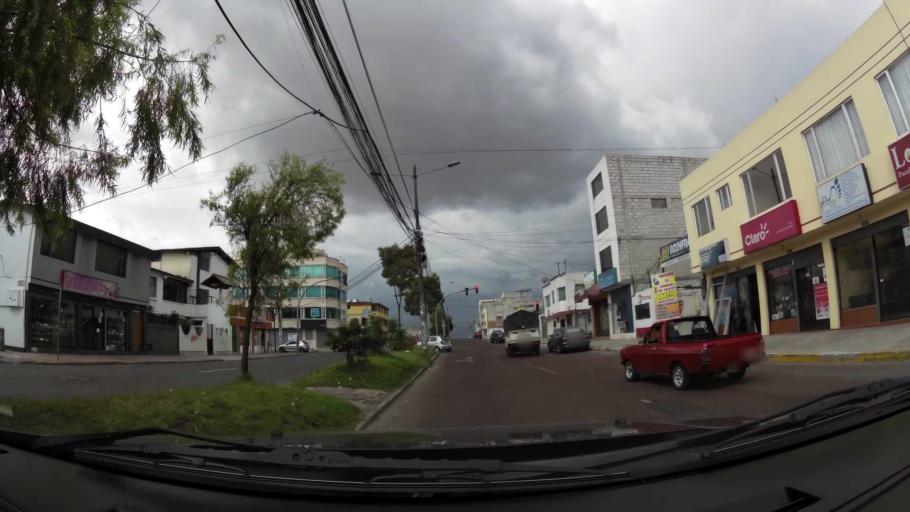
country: EC
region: Pichincha
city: Quito
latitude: -0.0914
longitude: -78.4698
